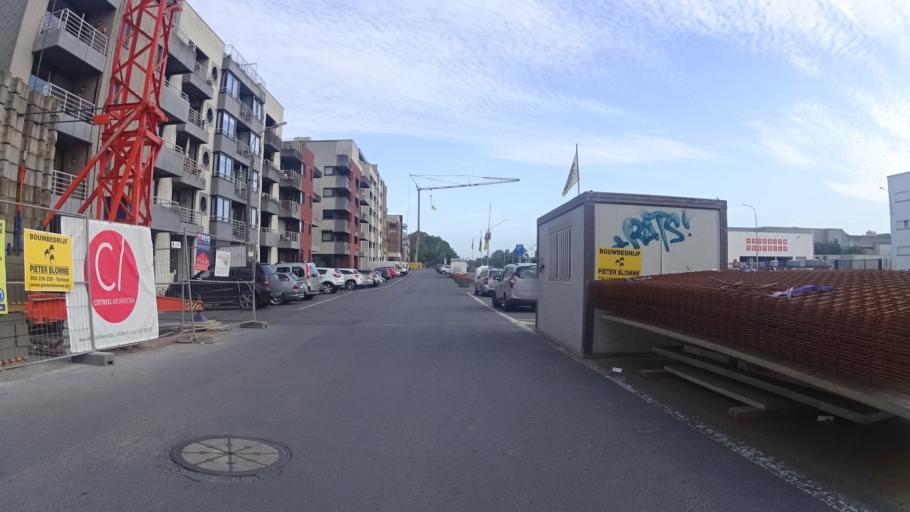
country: BE
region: Flanders
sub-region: Provincie West-Vlaanderen
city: Ieper
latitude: 50.8582
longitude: 2.8843
